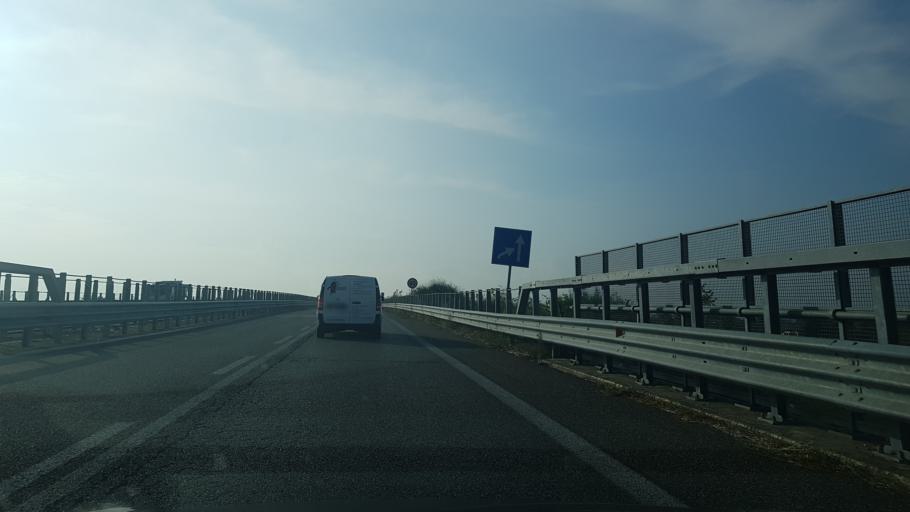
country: IT
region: Piedmont
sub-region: Provincia di Alessandria
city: Alessandria
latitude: 44.9342
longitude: 8.5945
